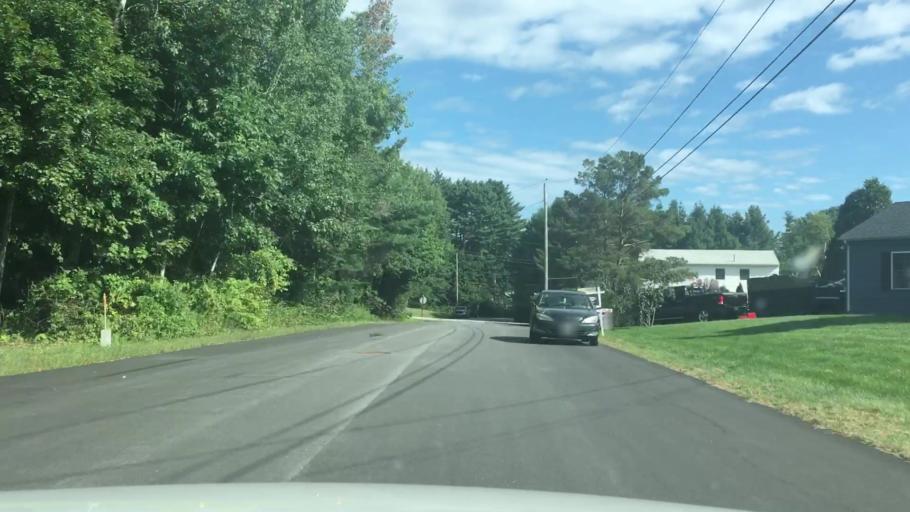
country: US
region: Maine
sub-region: Androscoggin County
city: Lewiston
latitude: 44.1156
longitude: -70.2011
